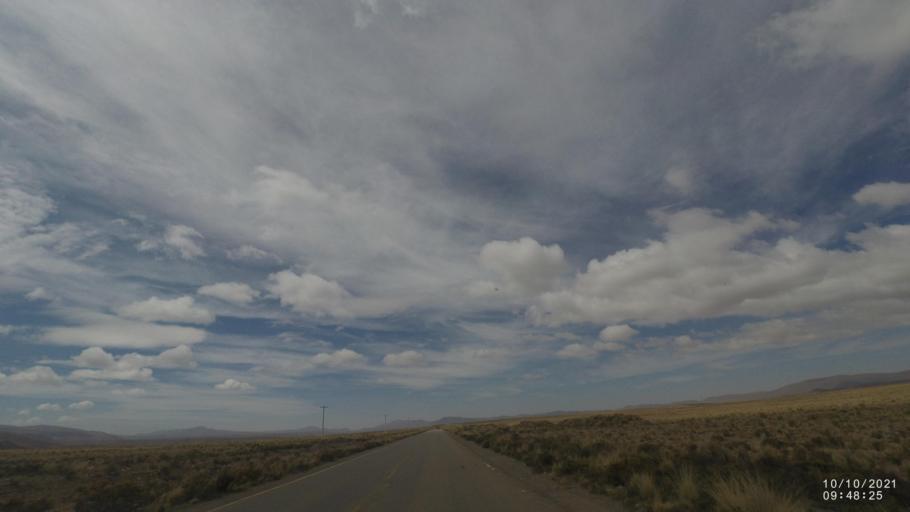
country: BO
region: La Paz
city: Quime
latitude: -17.2095
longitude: -67.3417
